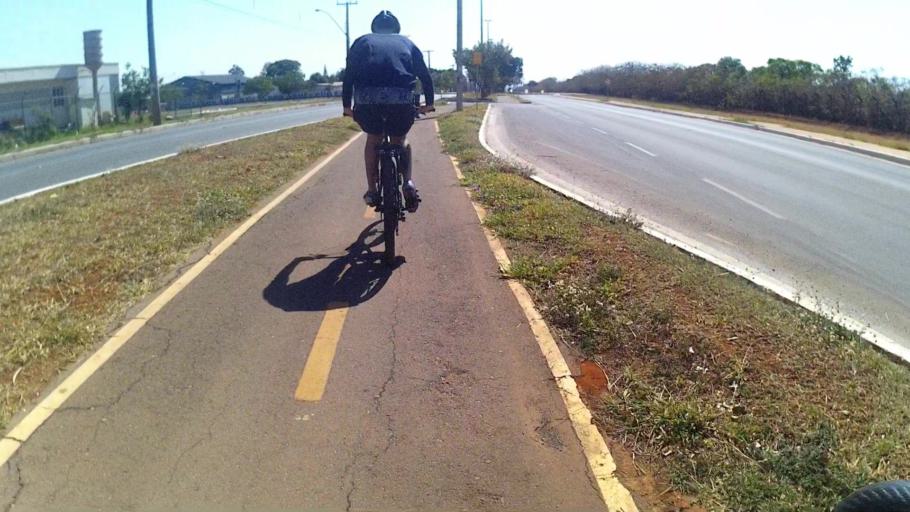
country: BR
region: Federal District
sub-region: Brasilia
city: Brasilia
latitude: -15.9071
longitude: -48.0479
